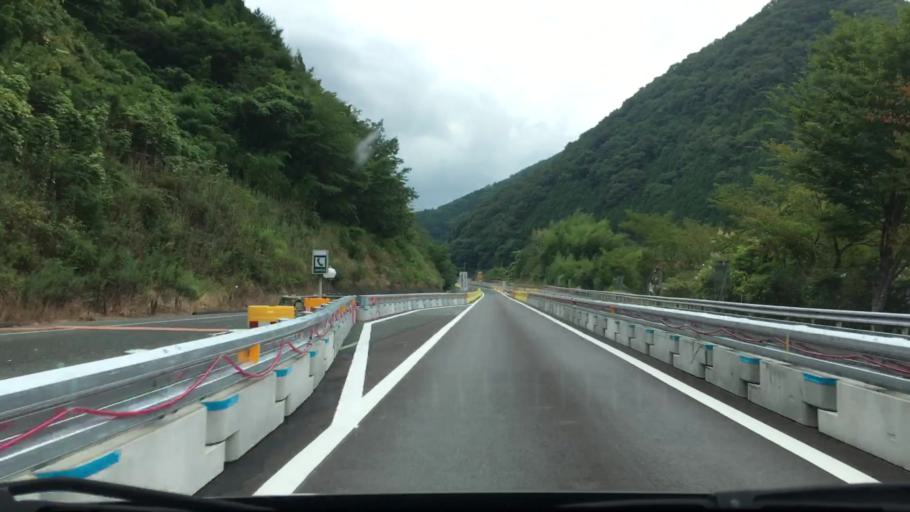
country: JP
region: Okayama
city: Niimi
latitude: 35.0026
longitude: 133.4027
